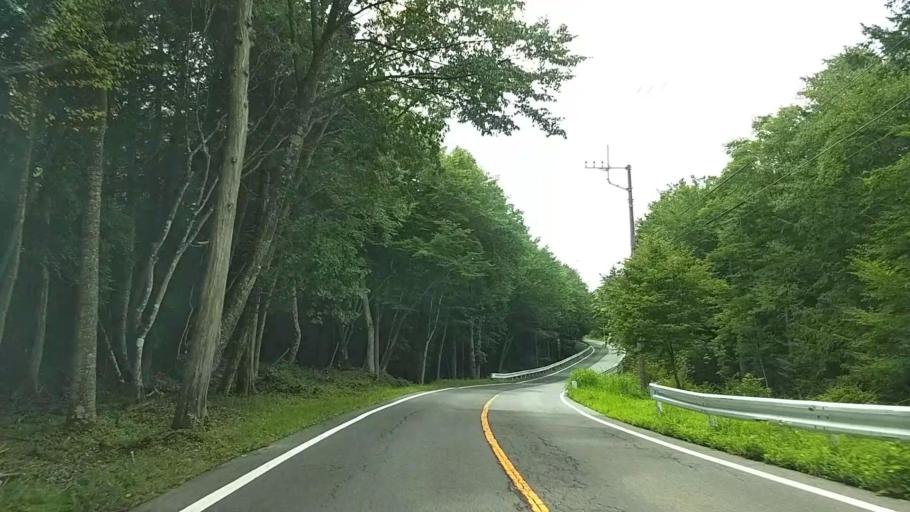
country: JP
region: Yamanashi
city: Fujikawaguchiko
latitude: 35.4833
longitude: 138.6636
